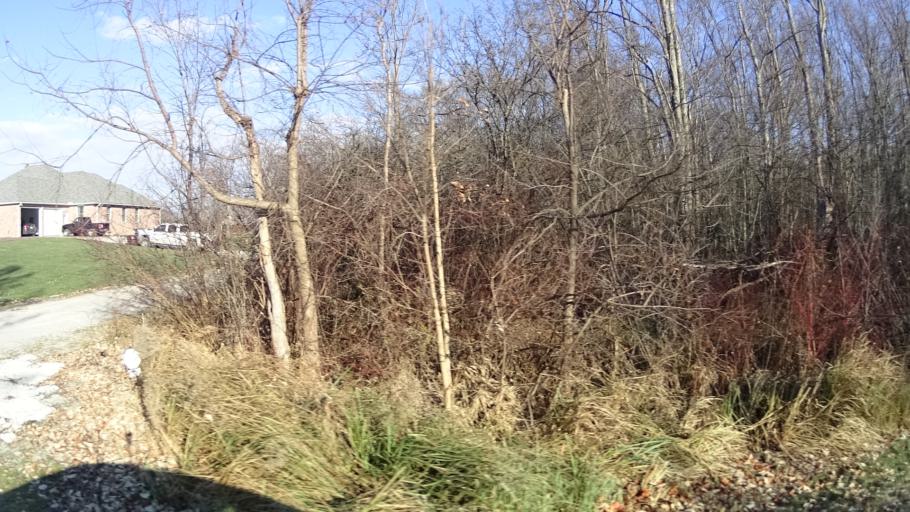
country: US
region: Ohio
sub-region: Lorain County
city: Oberlin
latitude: 41.2511
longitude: -82.2020
